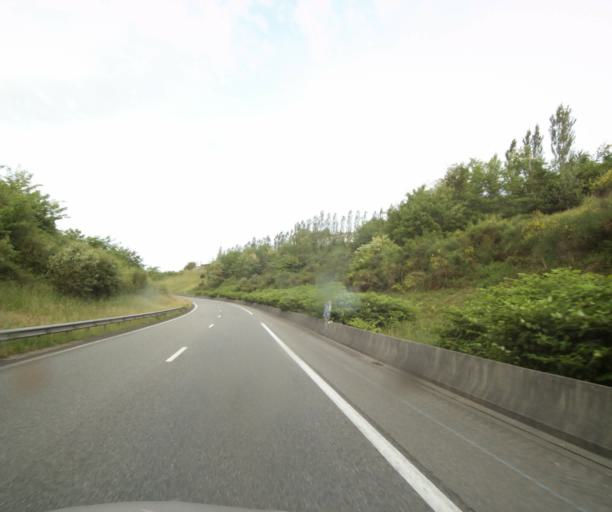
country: FR
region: Aquitaine
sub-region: Departement des Pyrenees-Atlantiques
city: Mouguerre
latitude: 43.4780
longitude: -1.4490
